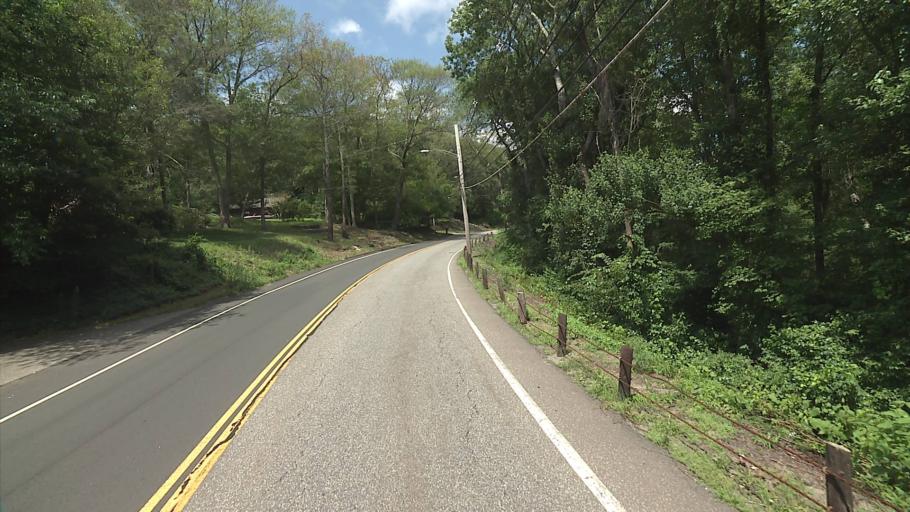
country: US
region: Connecticut
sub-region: Middlesex County
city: Essex Village
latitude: 41.3550
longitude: -72.4191
